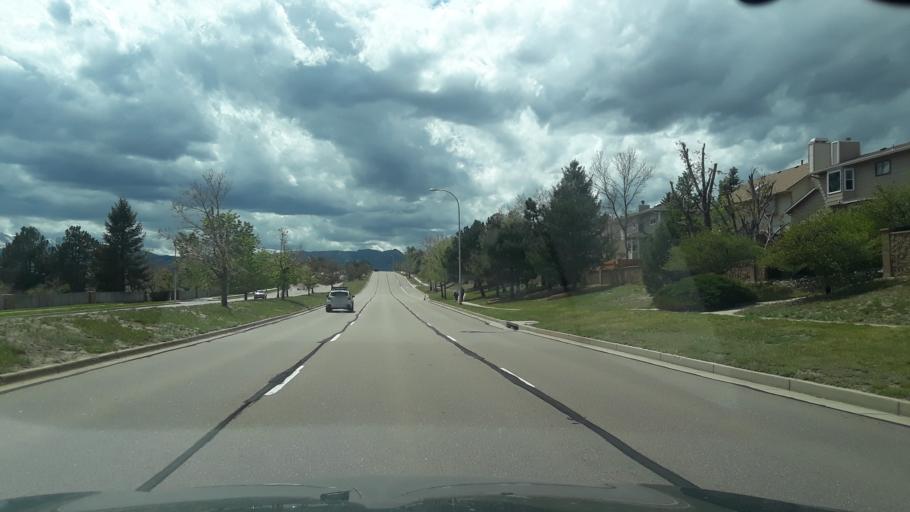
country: US
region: Colorado
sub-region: El Paso County
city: Black Forest
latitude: 38.9569
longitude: -104.7539
